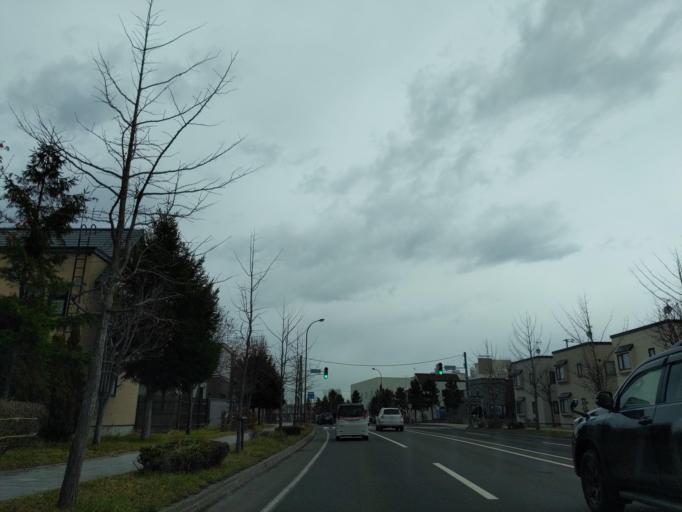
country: JP
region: Hokkaido
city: Sapporo
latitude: 43.1452
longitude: 141.3732
